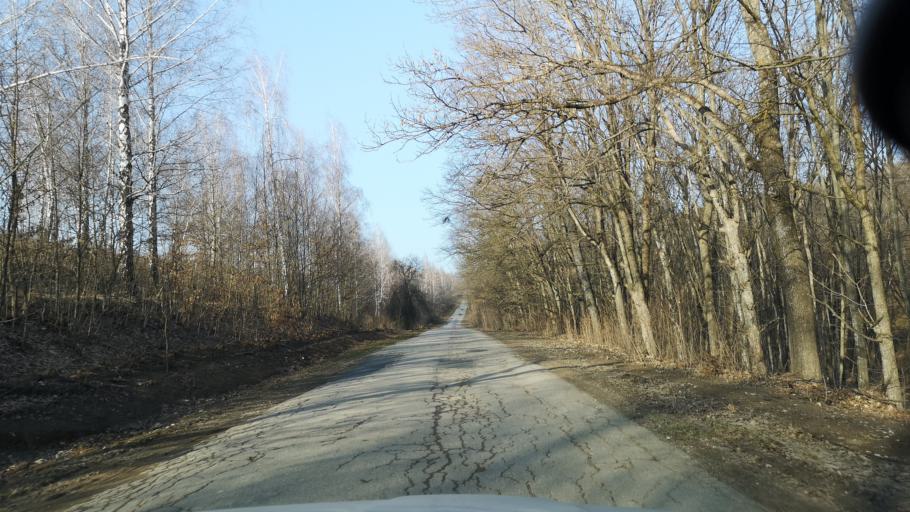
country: MD
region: Nisporeni
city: Nisporeni
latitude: 47.0926
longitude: 28.3158
